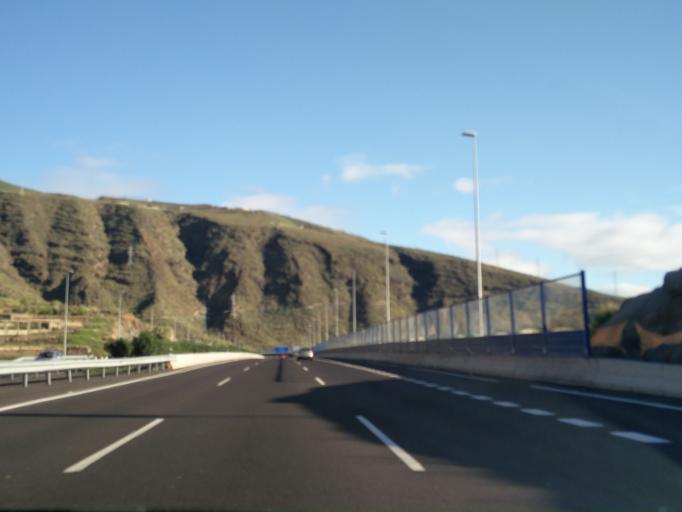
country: ES
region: Canary Islands
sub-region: Provincia de Santa Cruz de Tenerife
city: Candelaria
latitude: 28.3769
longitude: -16.3650
